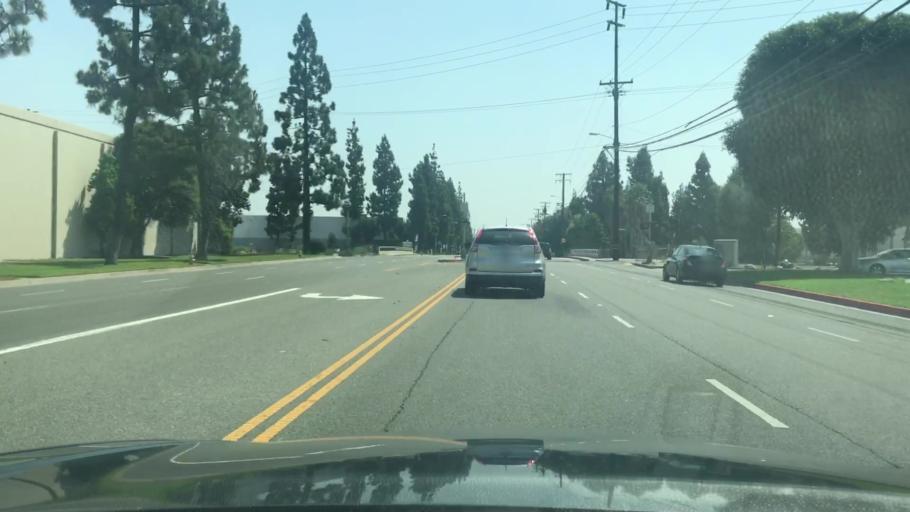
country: US
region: California
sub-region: Orange County
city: Buena Park
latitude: 33.8733
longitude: -118.0202
